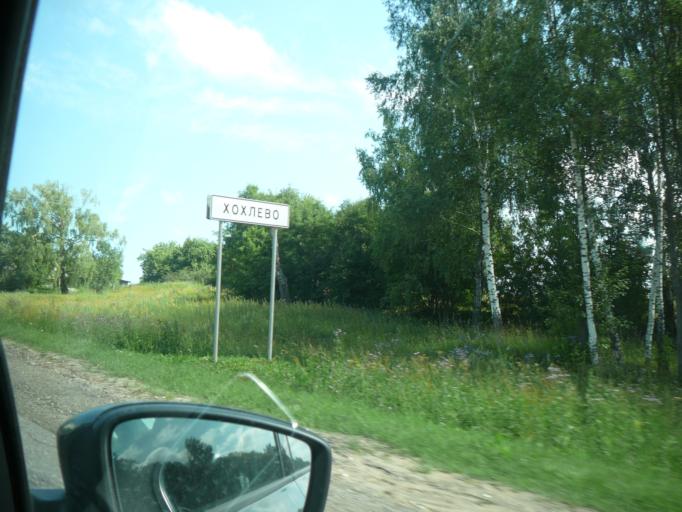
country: RU
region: Jaroslavl
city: Gavrilov-Yam
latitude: 57.3751
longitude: 39.9081
